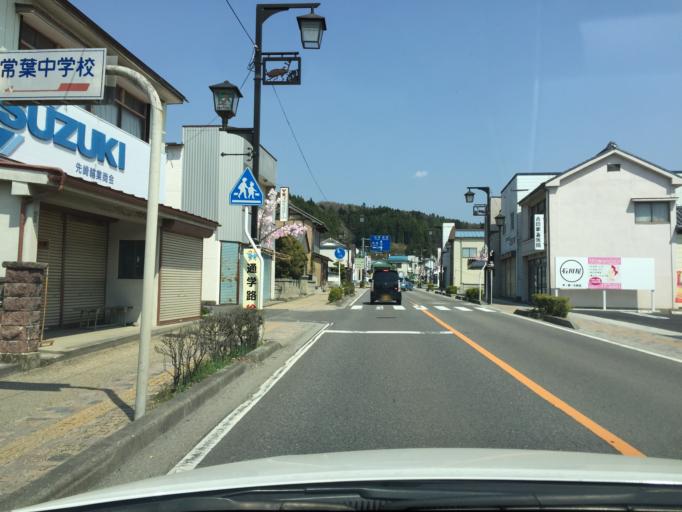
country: JP
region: Fukushima
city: Funehikimachi-funehiki
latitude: 37.4388
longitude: 140.6435
